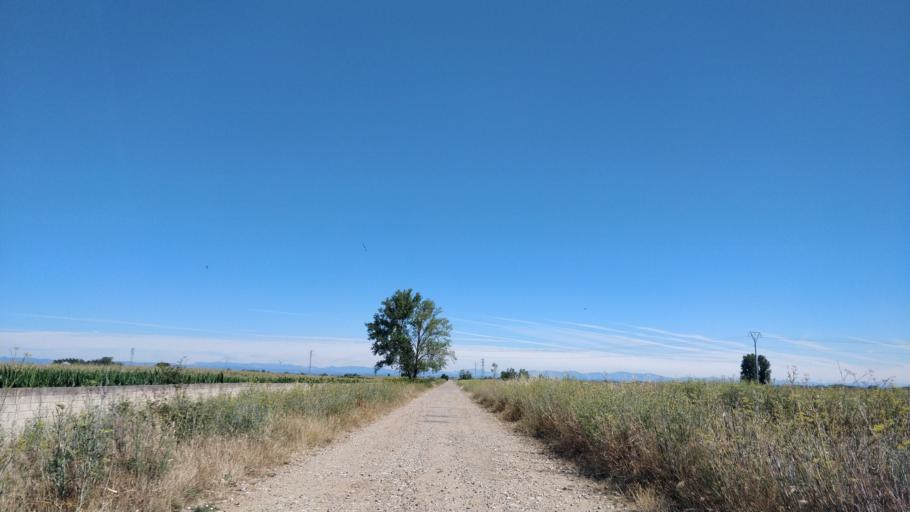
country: ES
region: Castille and Leon
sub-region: Provincia de Leon
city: Bustillo del Paramo
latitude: 42.4237
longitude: -5.8208
